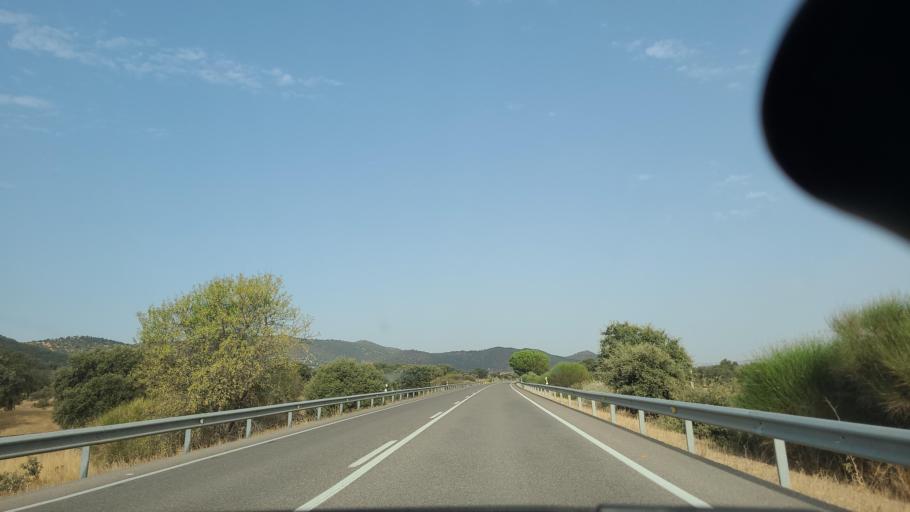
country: ES
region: Andalusia
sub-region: Province of Cordoba
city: Belmez
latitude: 38.2061
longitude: -5.1240
